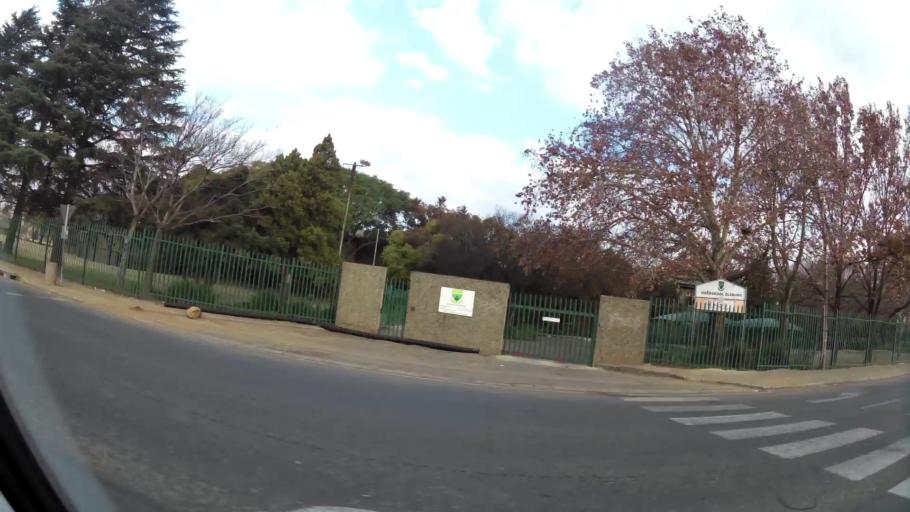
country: ZA
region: Gauteng
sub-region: Ekurhuleni Metropolitan Municipality
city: Germiston
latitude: -26.2509
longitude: 28.2007
